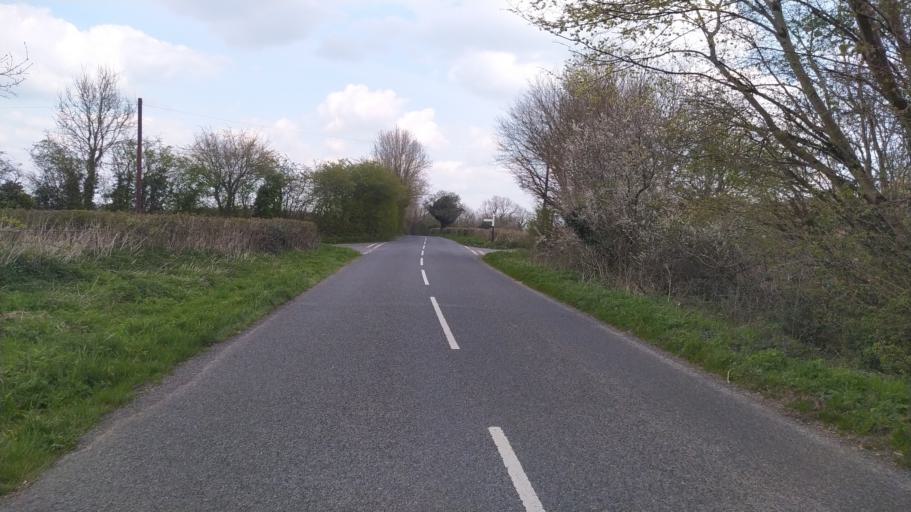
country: GB
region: England
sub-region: Bath and North East Somerset
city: Radstock
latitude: 51.2202
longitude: -2.4313
